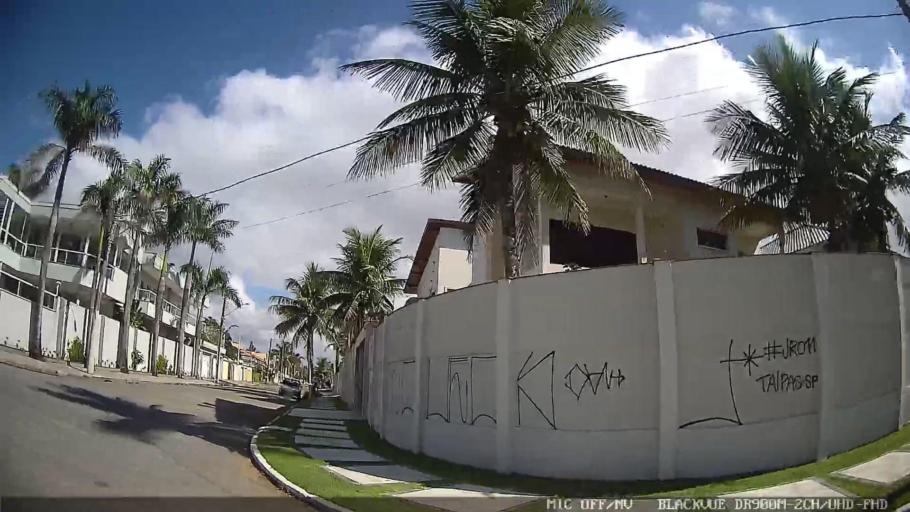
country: BR
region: Sao Paulo
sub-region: Peruibe
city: Peruibe
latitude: -24.2970
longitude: -46.9647
